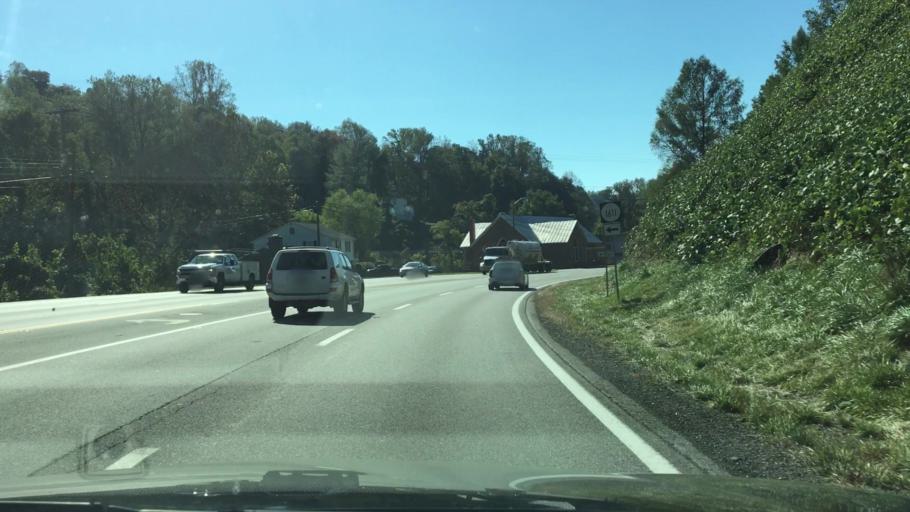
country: US
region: Virginia
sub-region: Roanoke County
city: Narrows
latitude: 37.1212
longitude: -79.9559
